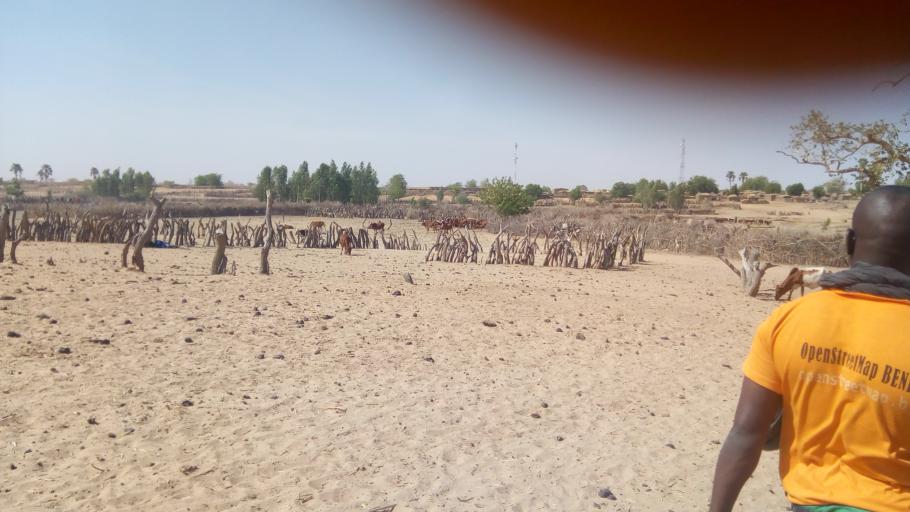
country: ML
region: Kayes
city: Diema
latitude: 14.5155
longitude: -8.8391
